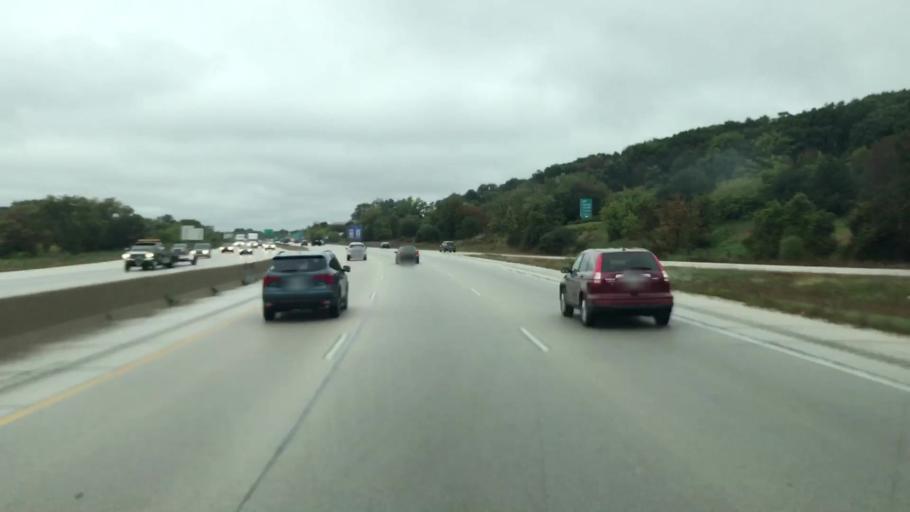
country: US
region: Wisconsin
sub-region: Waukesha County
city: Waukesha
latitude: 43.0490
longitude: -88.2103
